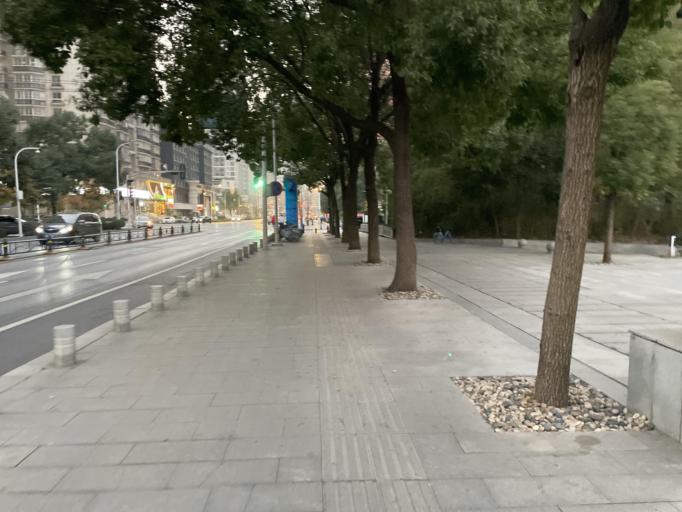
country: CN
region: Hubei
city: Jiang'an
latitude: 30.5532
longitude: 114.3435
